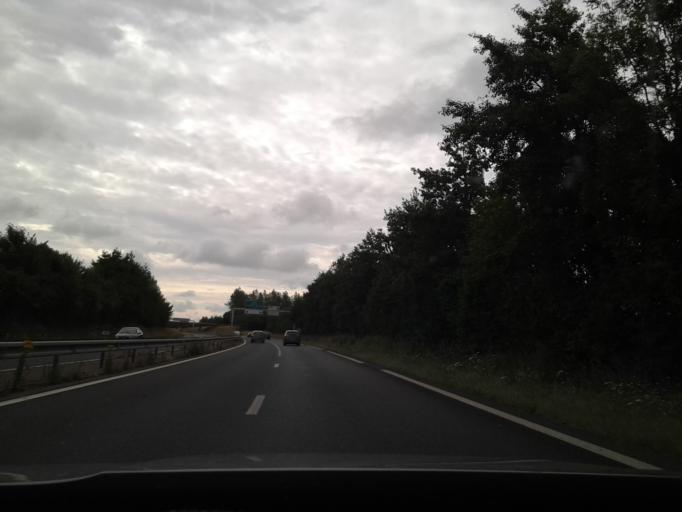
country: FR
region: Lower Normandy
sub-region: Departement de la Manche
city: Saint-Hilaire-Petitville
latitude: 49.3067
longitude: -1.2154
